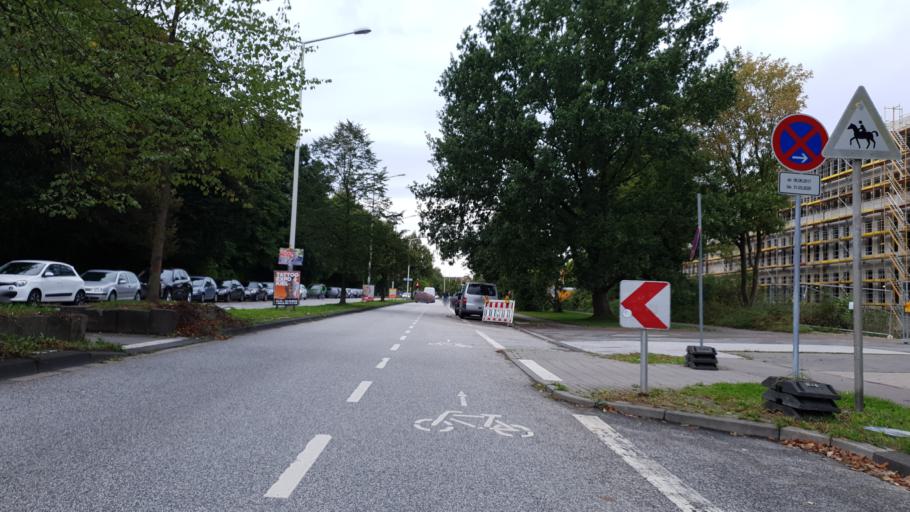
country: DE
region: Schleswig-Holstein
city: Kronshagen
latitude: 54.3435
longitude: 10.1105
